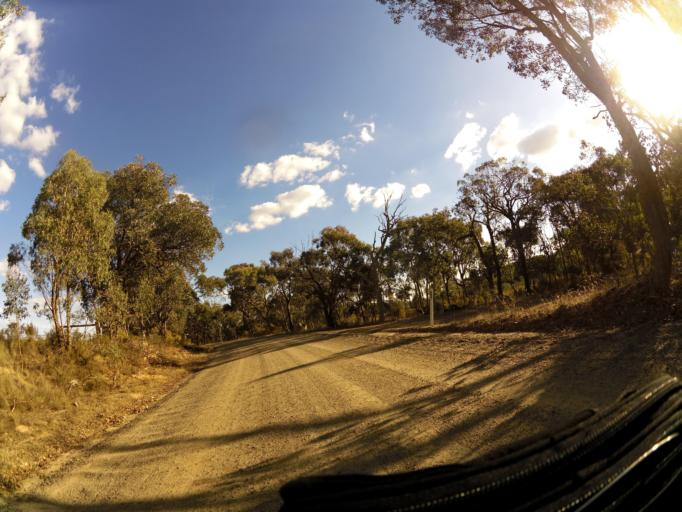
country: AU
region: Victoria
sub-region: Greater Bendigo
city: Kennington
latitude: -37.0216
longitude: 144.8009
